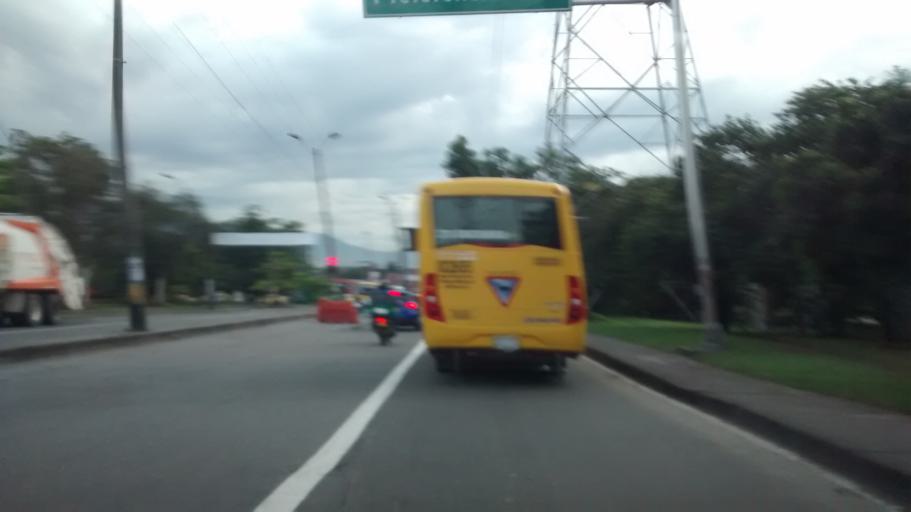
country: CO
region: Antioquia
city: Medellin
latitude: 6.2791
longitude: -75.5727
